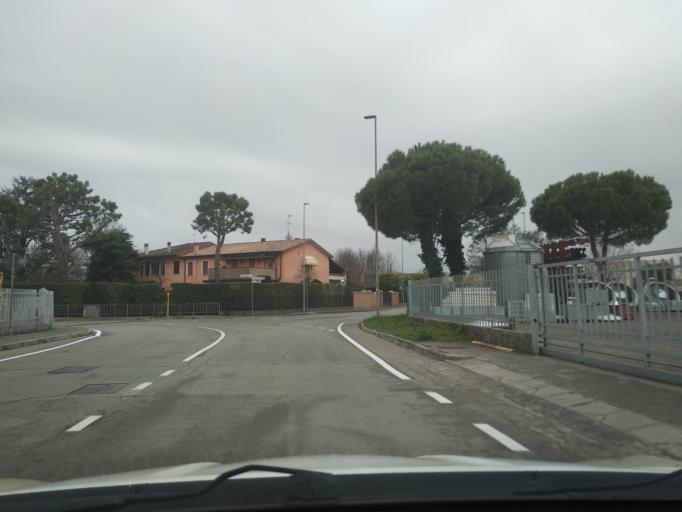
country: IT
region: Veneto
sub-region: Provincia di Padova
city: Rubano
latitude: 45.4215
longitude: 11.7923
